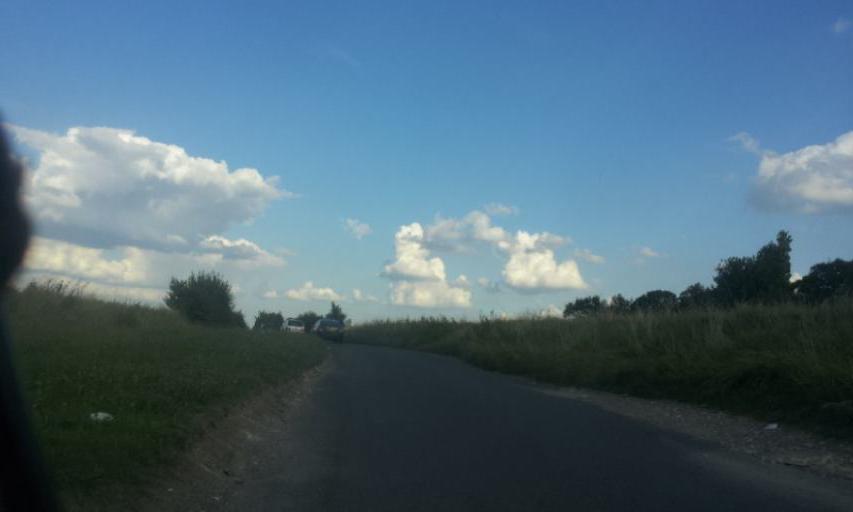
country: GB
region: England
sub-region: Kent
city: Dartford
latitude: 51.4051
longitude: 0.2286
